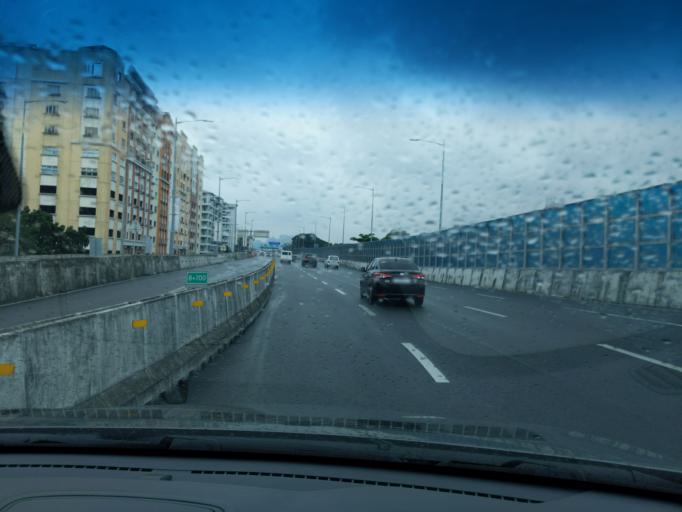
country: PH
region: Metro Manila
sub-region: Makati City
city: Makati City
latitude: 14.5172
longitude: 121.0201
